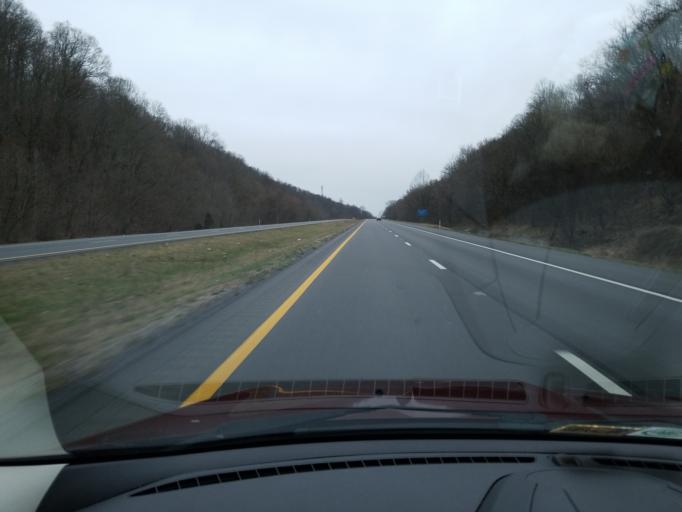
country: US
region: Virginia
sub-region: Giles County
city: Narrows
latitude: 37.3627
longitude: -80.8748
